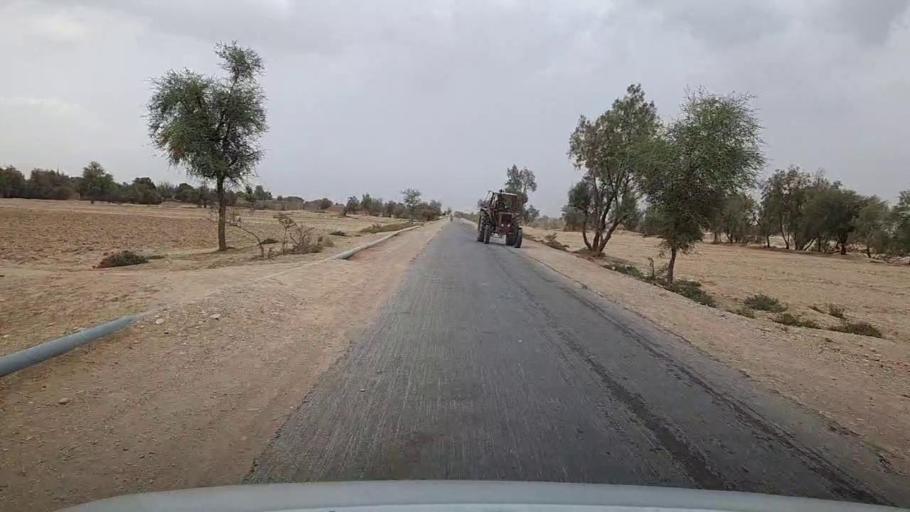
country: PK
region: Sindh
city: Sehwan
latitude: 26.3265
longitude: 67.7257
